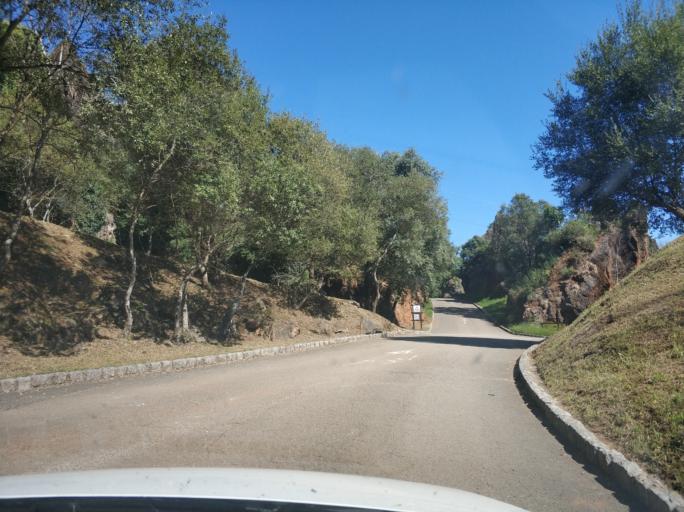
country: ES
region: Cantabria
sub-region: Provincia de Cantabria
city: Penagos
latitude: 43.3589
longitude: -3.8335
